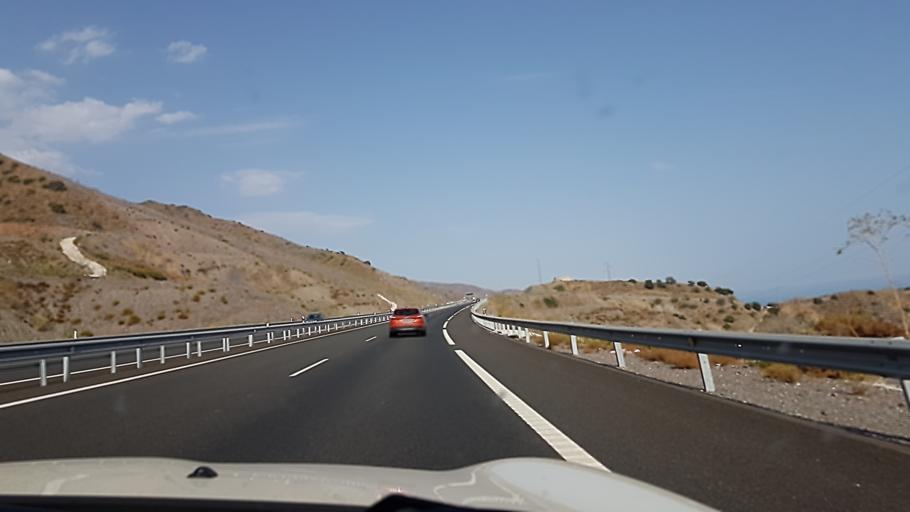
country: ES
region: Andalusia
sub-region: Provincia de Granada
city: Sorvilan
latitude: 36.7526
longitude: -3.2775
